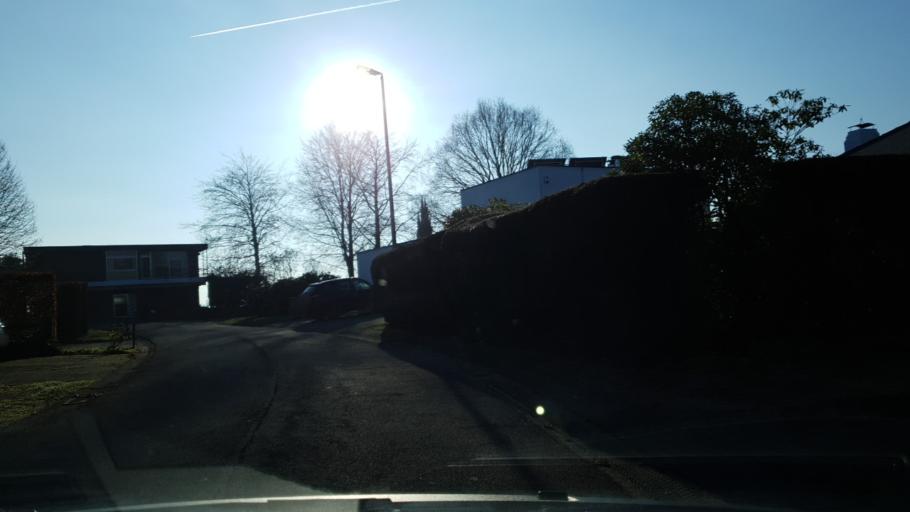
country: BE
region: Flanders
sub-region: Provincie Vlaams-Brabant
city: Herent
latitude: 50.8864
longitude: 4.6545
